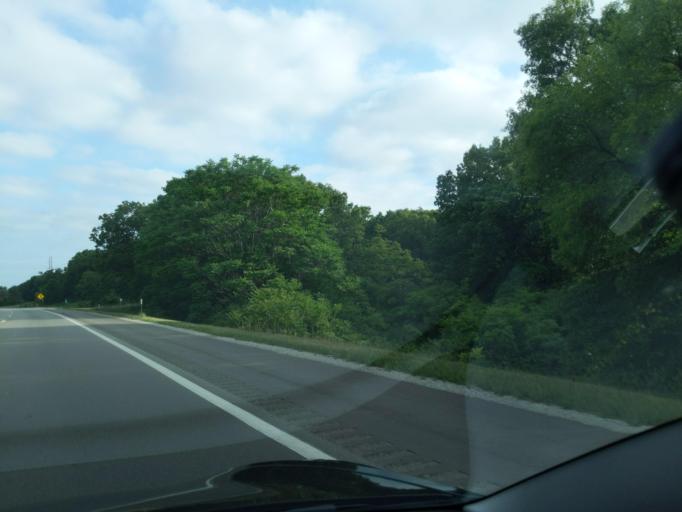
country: US
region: Michigan
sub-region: Muskegon County
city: Muskegon
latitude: 43.2556
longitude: -86.2066
